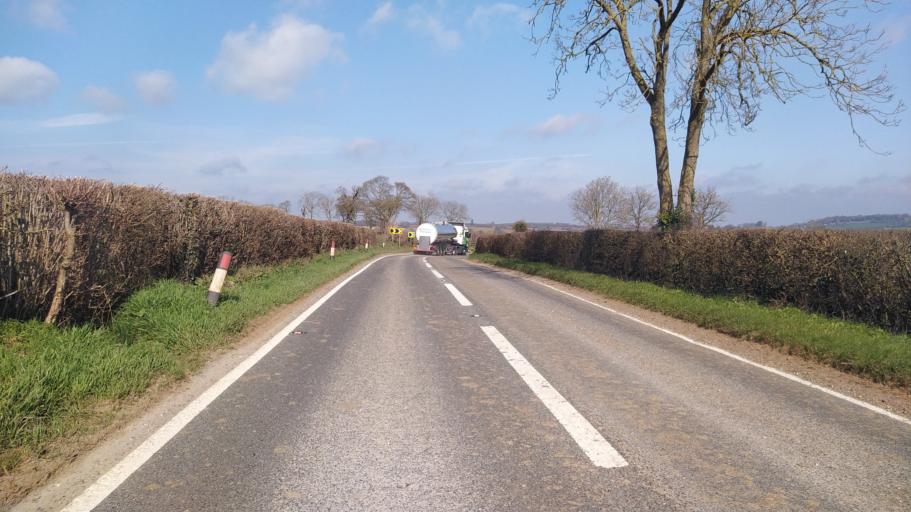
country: GB
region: England
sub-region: Somerset
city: Merriott
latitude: 50.9239
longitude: -2.7731
